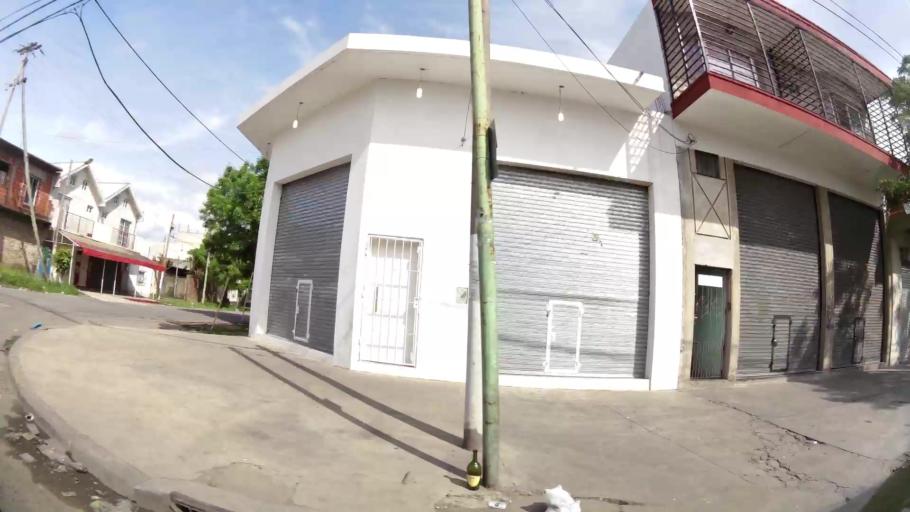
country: AR
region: Buenos Aires
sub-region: Partido de Quilmes
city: Quilmes
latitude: -34.7599
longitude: -58.2413
